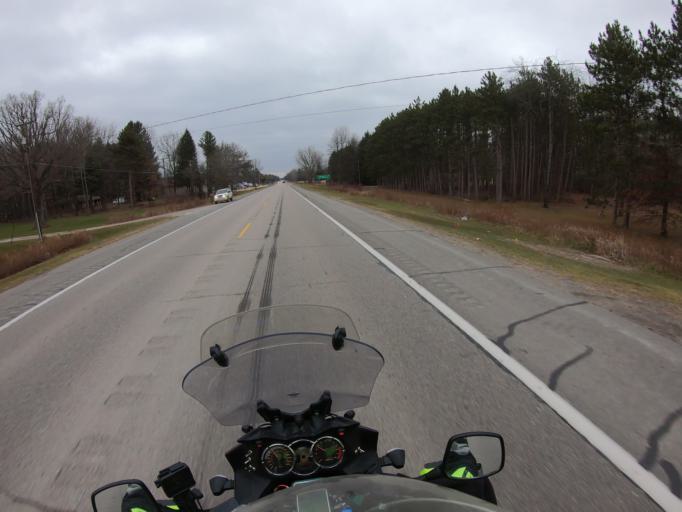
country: US
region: Michigan
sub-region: Saginaw County
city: Saint Charles
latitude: 43.3198
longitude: -84.1417
